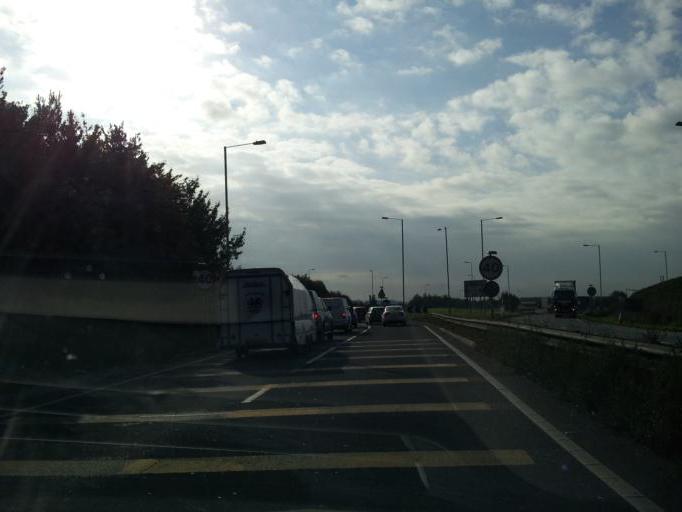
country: GB
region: England
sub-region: Northamptonshire
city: Towcester
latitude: 52.1301
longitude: -1.0035
